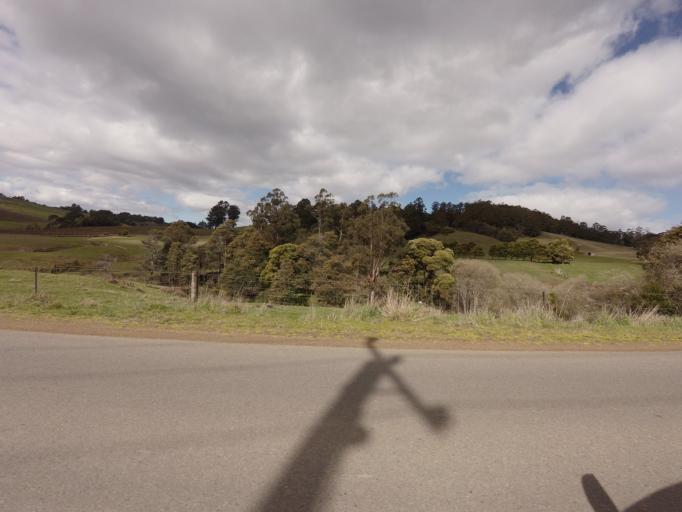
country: AU
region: Tasmania
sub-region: Huon Valley
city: Geeveston
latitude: -43.2427
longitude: 146.9918
